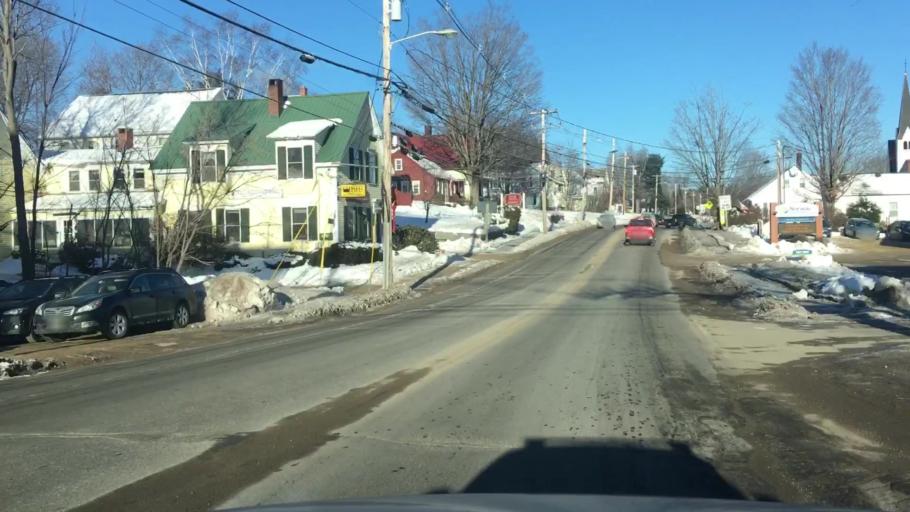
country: US
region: Maine
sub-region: Oxford County
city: South Paris
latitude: 44.2242
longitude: -70.5132
